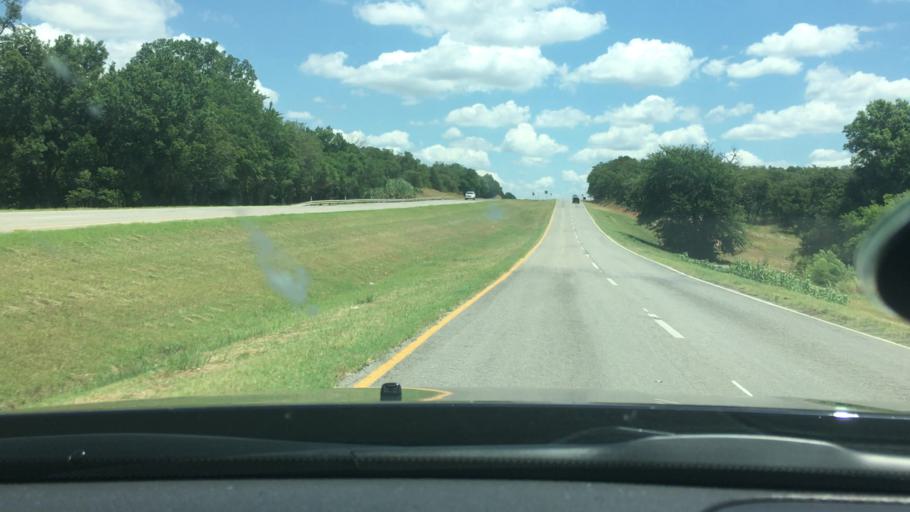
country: US
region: Oklahoma
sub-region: Carter County
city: Wilson
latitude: 34.1728
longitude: -97.3512
